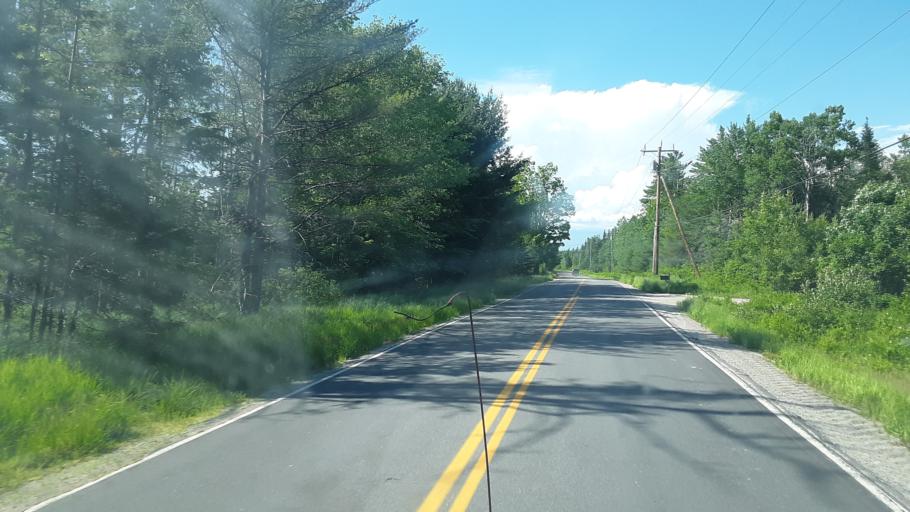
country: US
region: Maine
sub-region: Washington County
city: Cherryfield
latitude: 44.6450
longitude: -67.9468
